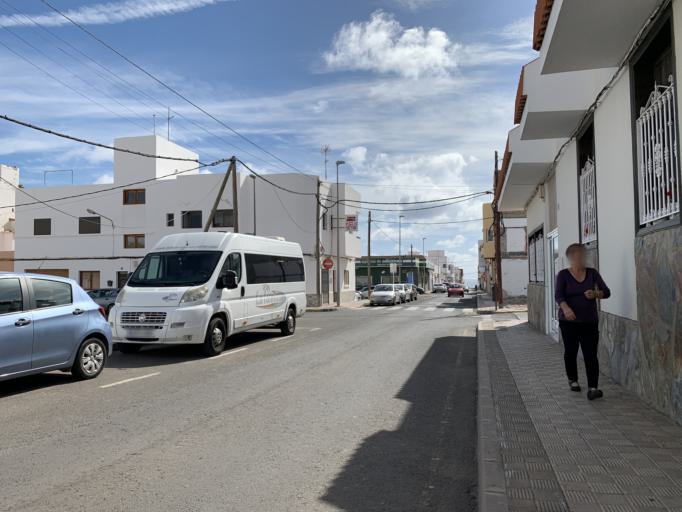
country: ES
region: Canary Islands
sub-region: Provincia de Las Palmas
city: Puerto del Rosario
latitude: 28.5050
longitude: -13.8497
